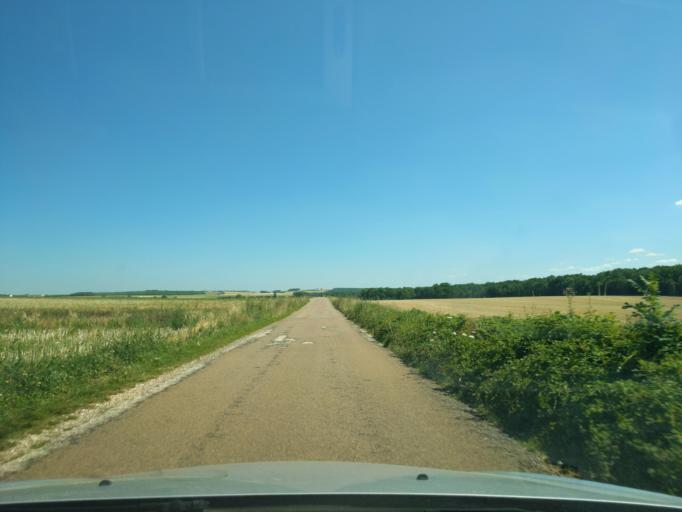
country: FR
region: Bourgogne
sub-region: Departement de la Cote-d'Or
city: Ruffey-les-Echirey
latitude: 47.3910
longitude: 5.0792
